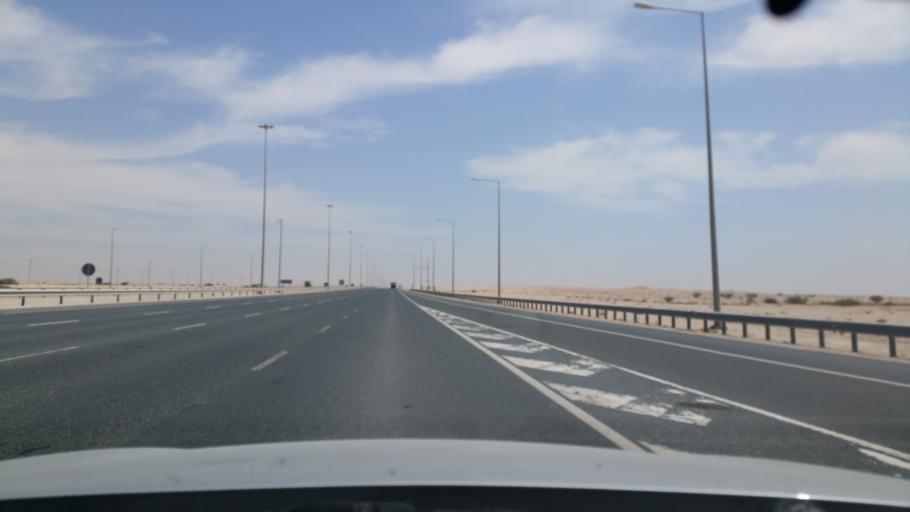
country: QA
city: Umm Bab
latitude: 25.0153
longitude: 51.0532
